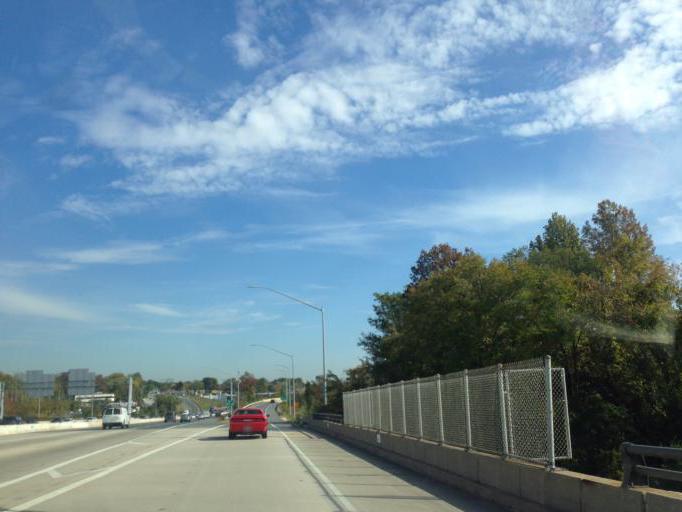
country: US
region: Maryland
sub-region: Baltimore County
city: Lutherville
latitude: 39.4190
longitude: -76.6369
